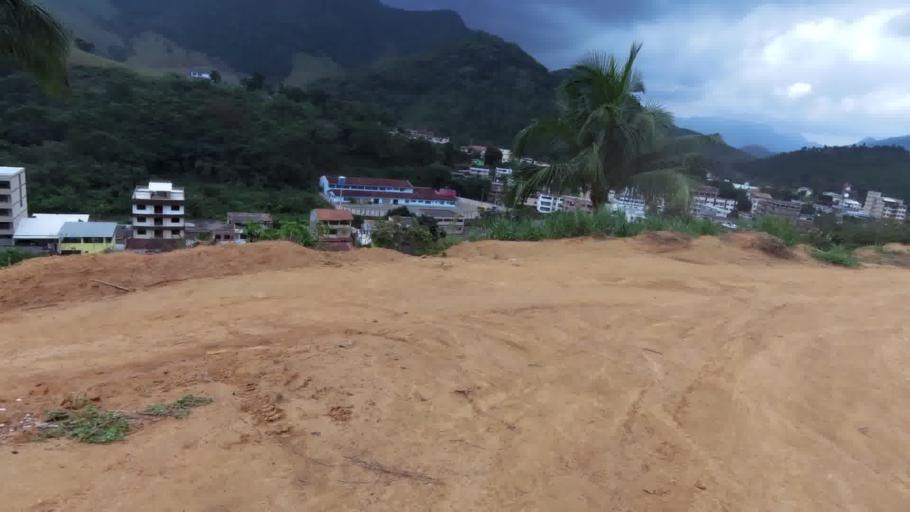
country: BR
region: Espirito Santo
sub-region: Alfredo Chaves
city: Alfredo Chaves
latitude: -20.6375
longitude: -40.7540
